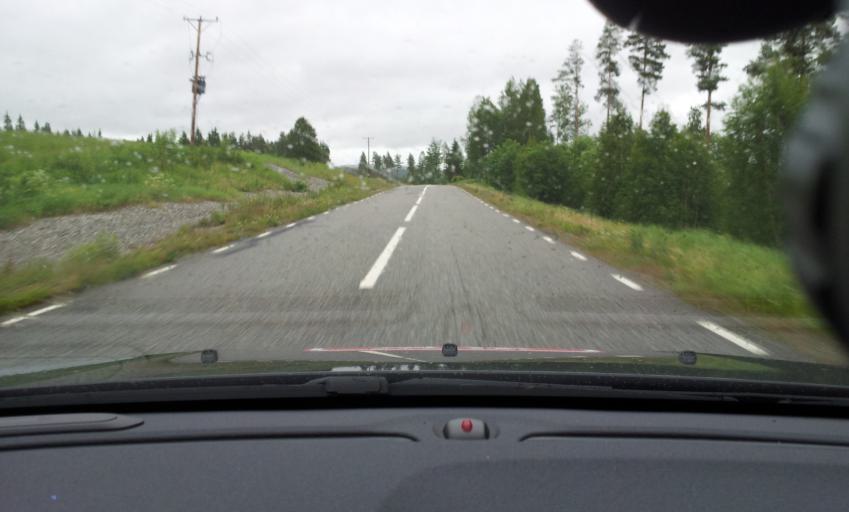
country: SE
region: Jaemtland
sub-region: Ragunda Kommun
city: Hammarstrand
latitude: 63.2645
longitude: 15.8568
